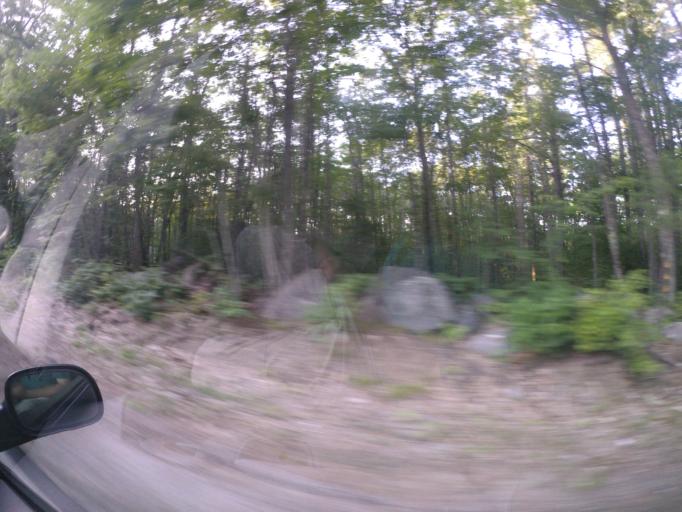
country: US
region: Maine
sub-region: Cumberland County
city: Raymond
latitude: 43.8948
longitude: -70.4469
